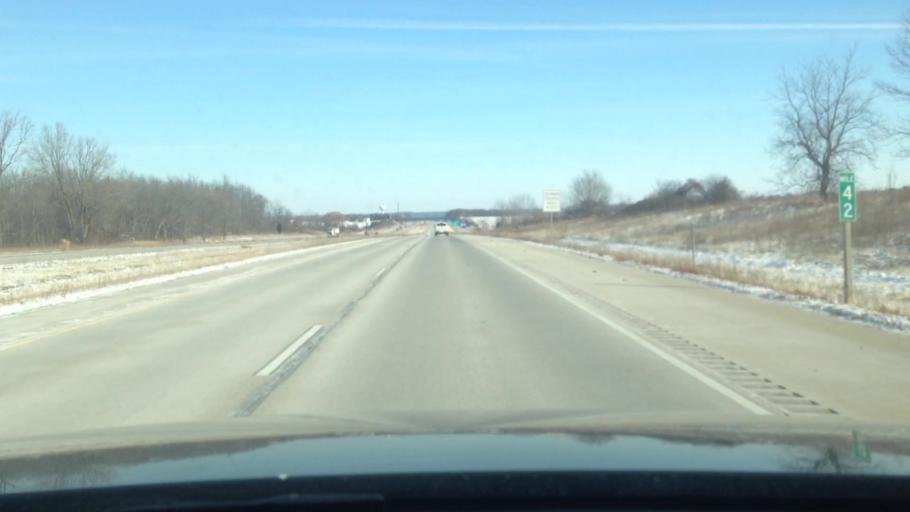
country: US
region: Wisconsin
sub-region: Walworth County
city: Potter Lake
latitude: 42.8324
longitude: -88.3470
